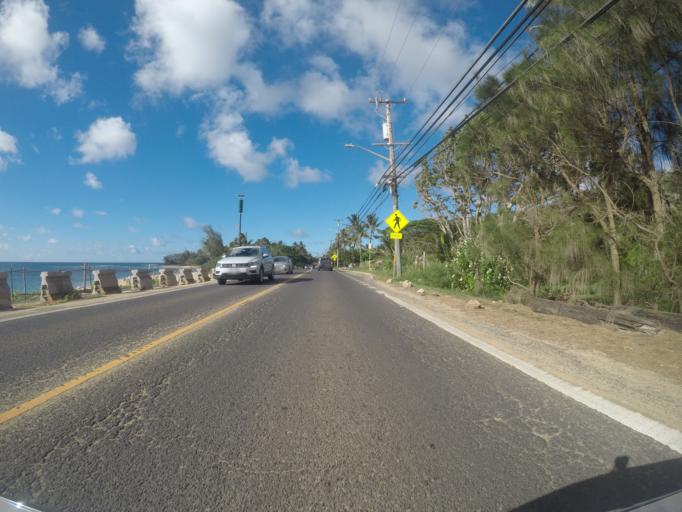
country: US
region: Hawaii
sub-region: Honolulu County
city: Pupukea
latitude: 21.6738
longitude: -158.0403
